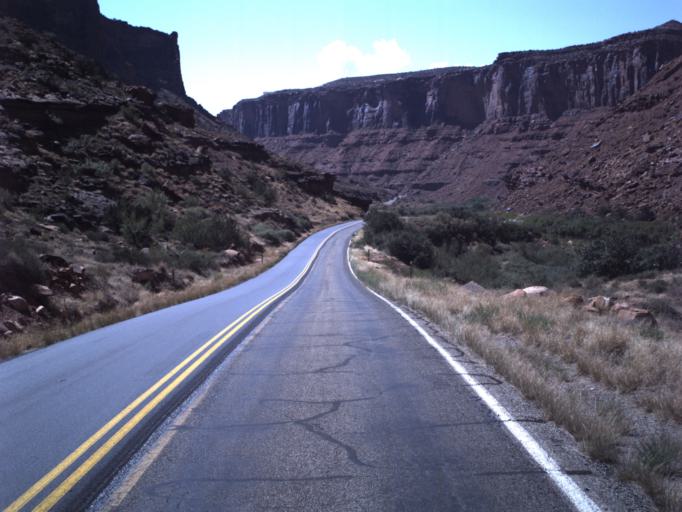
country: US
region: Utah
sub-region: Grand County
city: Moab
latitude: 38.6793
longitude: -109.4837
